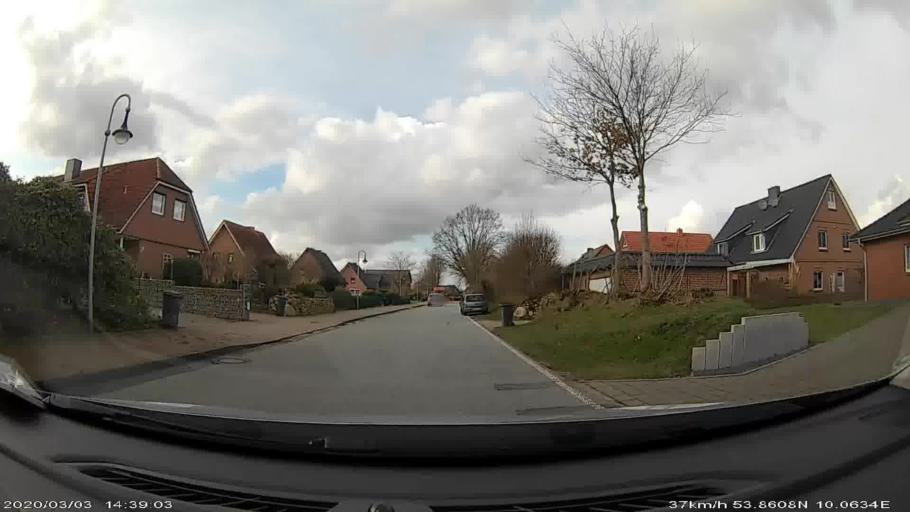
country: DE
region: Schleswig-Holstein
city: Struvenhutten
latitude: 53.8609
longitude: 10.0634
